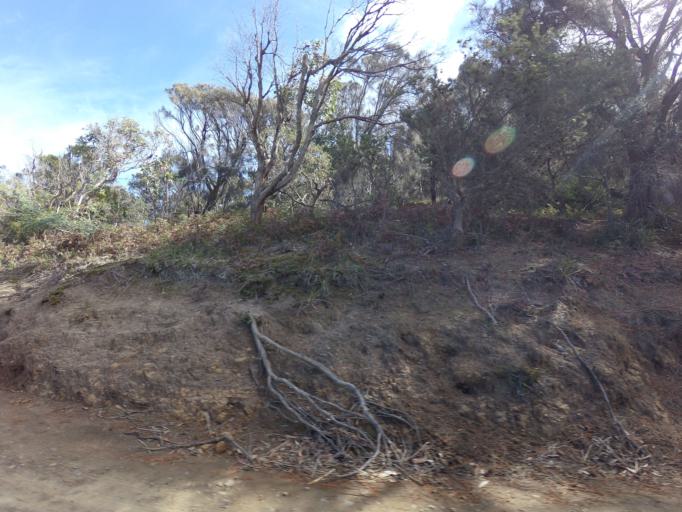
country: AU
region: Tasmania
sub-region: Clarence
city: Sandford
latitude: -43.0832
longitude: 147.6725
